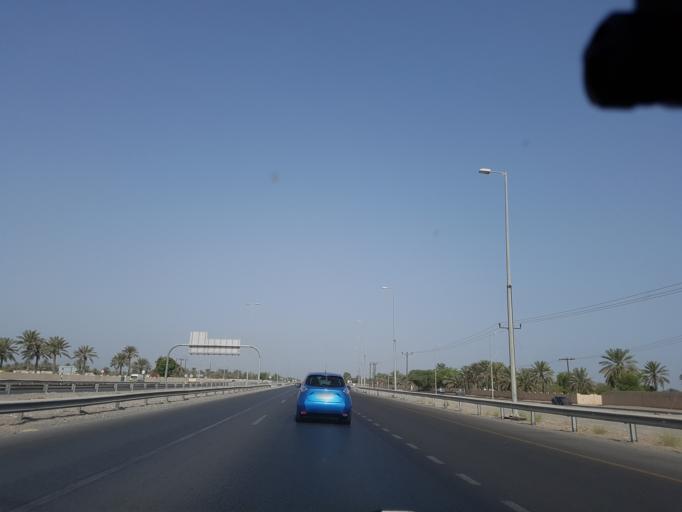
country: OM
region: Al Batinah
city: Barka'
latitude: 23.6710
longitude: 57.8679
